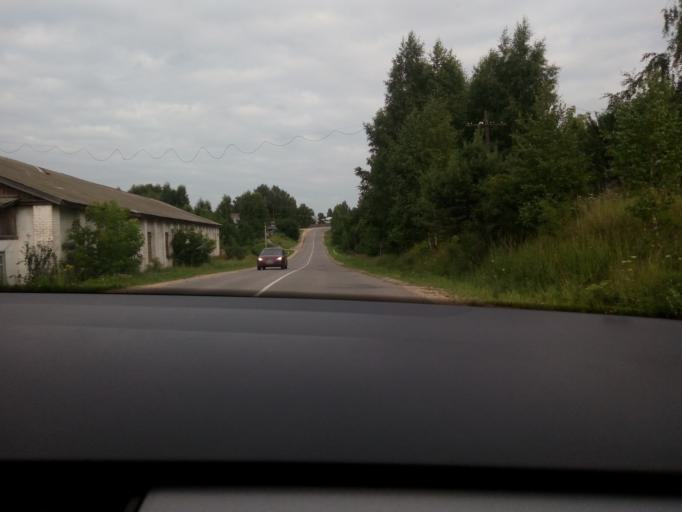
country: RU
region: Nizjnij Novgorod
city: Voskresenskoye
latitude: 56.8104
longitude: 45.4471
